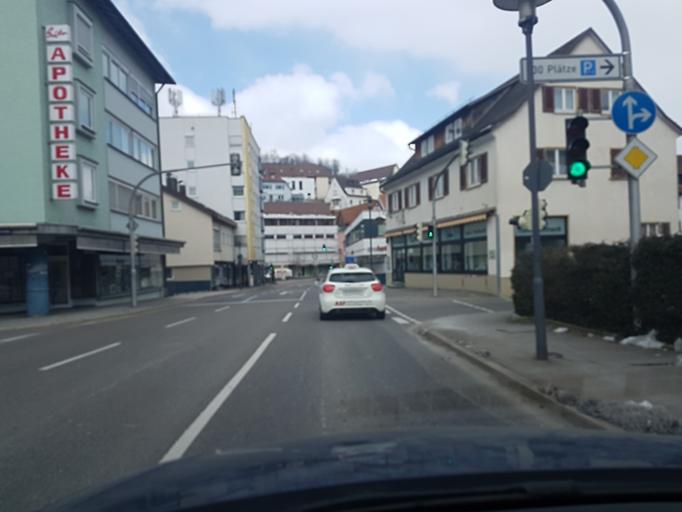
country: DE
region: Baden-Wuerttemberg
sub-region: Karlsruhe Region
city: Horb am Neckar
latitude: 48.4433
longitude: 8.6910
